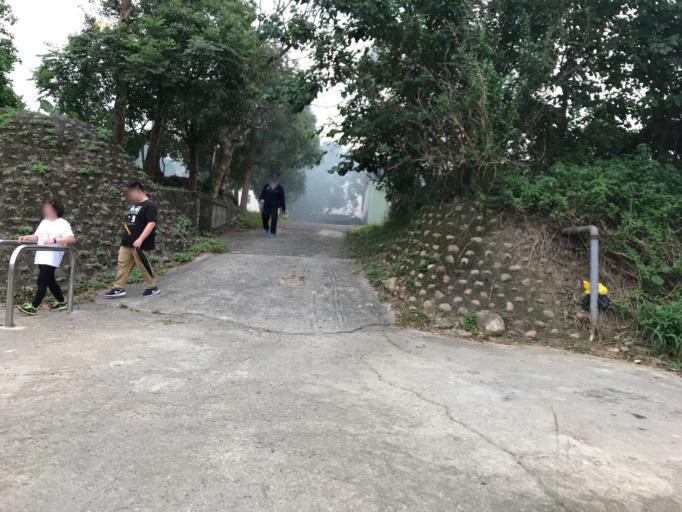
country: TW
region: Taiwan
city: Daxi
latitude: 24.7865
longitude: 121.1772
